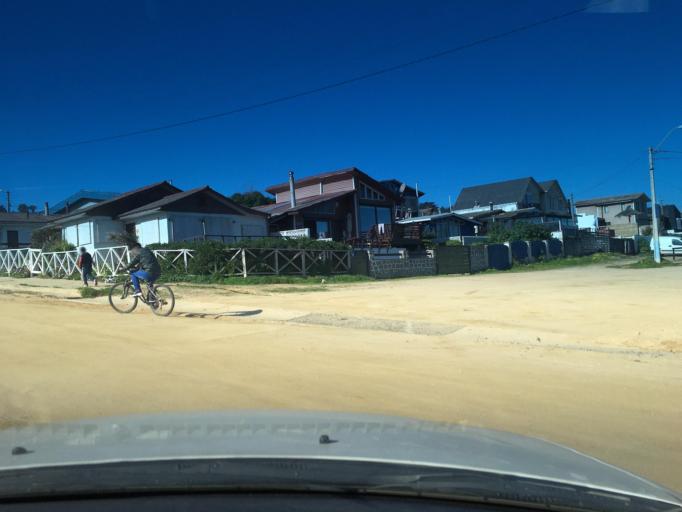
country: CL
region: Valparaiso
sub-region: San Antonio Province
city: El Tabo
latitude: -33.4598
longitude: -71.6599
